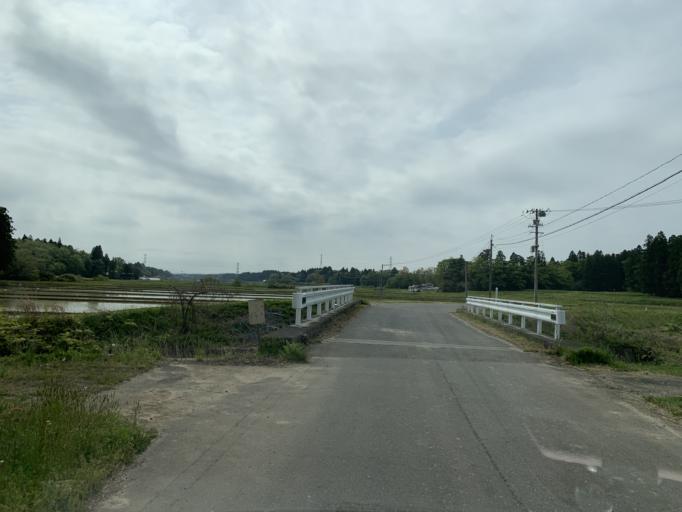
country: JP
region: Iwate
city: Ichinoseki
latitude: 38.8626
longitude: 141.0617
